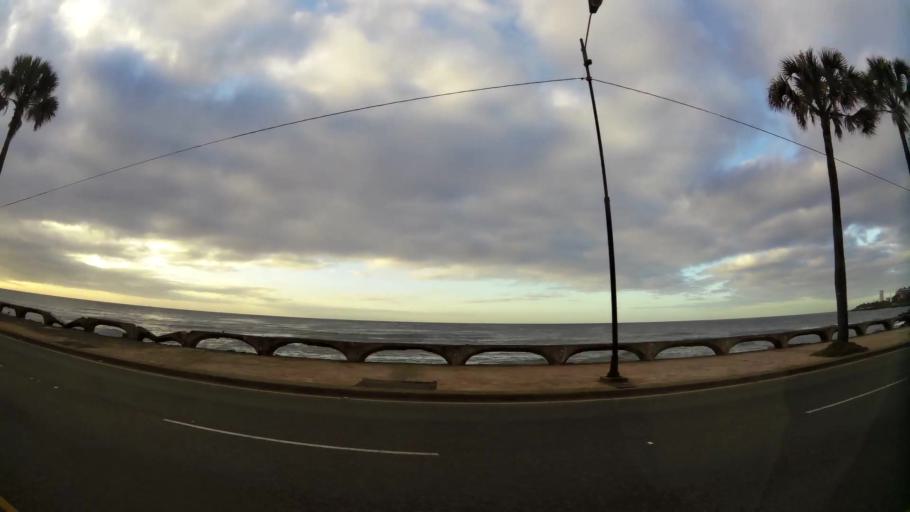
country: DO
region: Nacional
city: Ciudad Nueva
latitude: 18.4558
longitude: -69.9154
